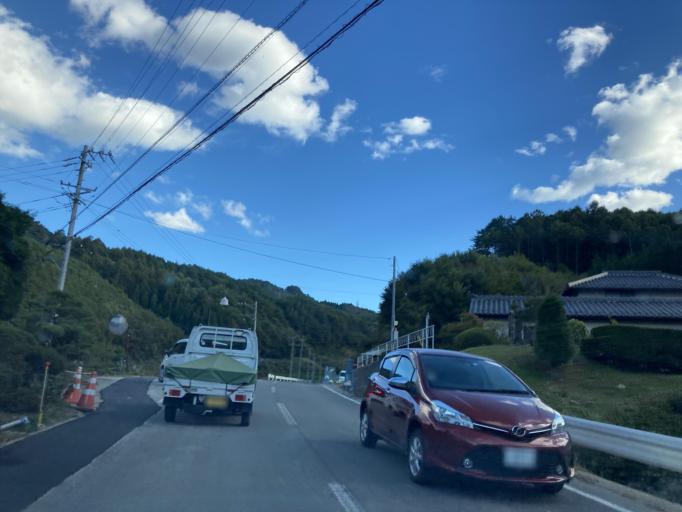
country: JP
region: Nagano
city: Ueda
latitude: 36.4159
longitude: 138.1040
